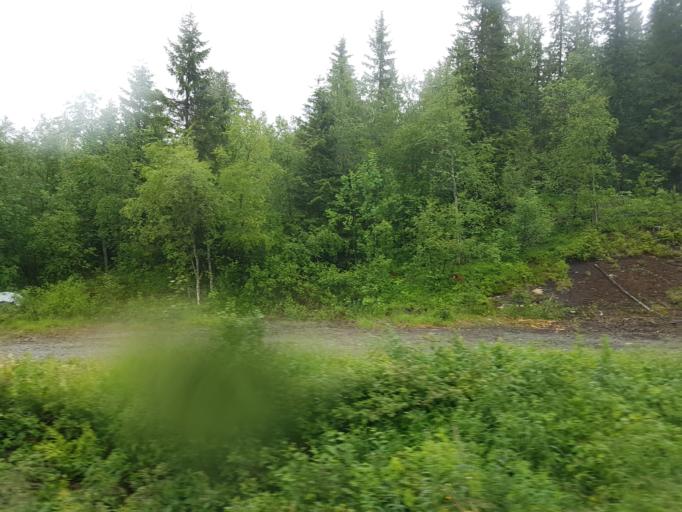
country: NO
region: Nord-Trondelag
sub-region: Stjordal
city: Stjordalshalsen
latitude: 63.3960
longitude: 10.9600
